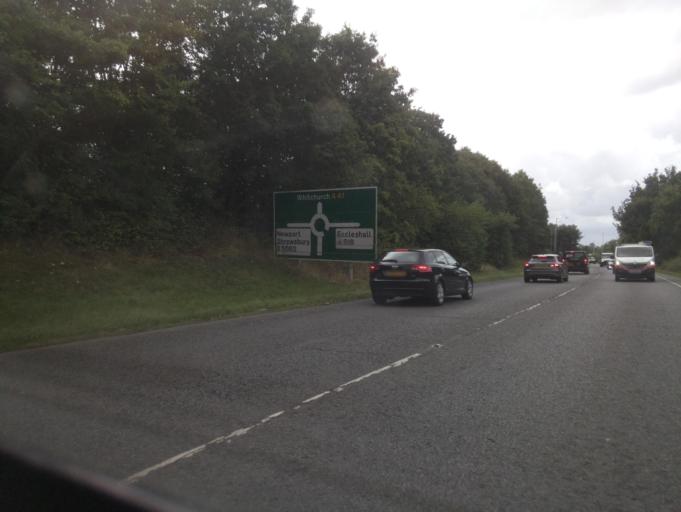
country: GB
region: England
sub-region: Telford and Wrekin
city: Newport
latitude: 52.7816
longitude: -2.3702
